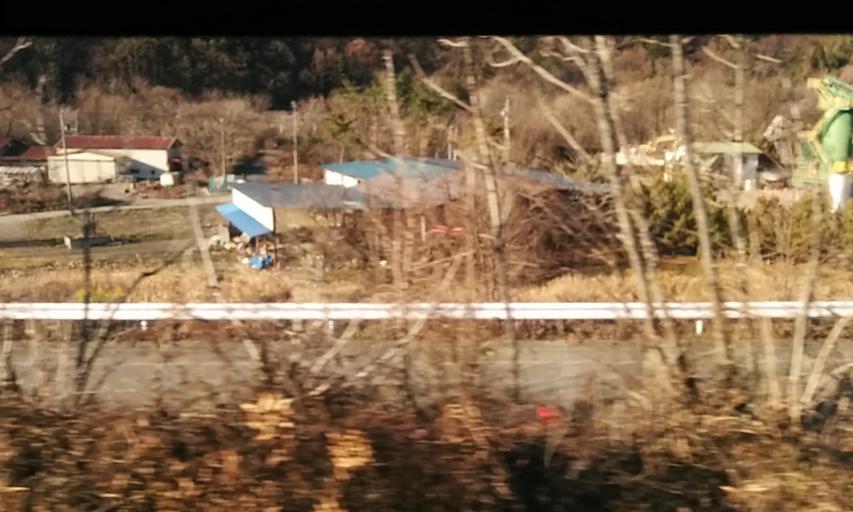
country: JP
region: Nagano
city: Ina
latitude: 35.8759
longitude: 137.7500
